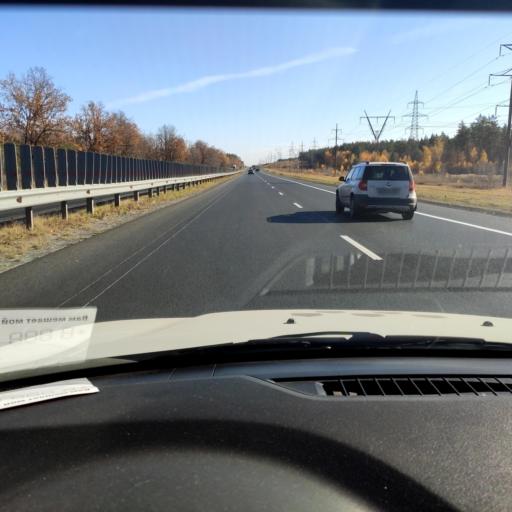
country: RU
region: Samara
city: Pribrezhnyy
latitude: 53.5159
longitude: 49.8761
